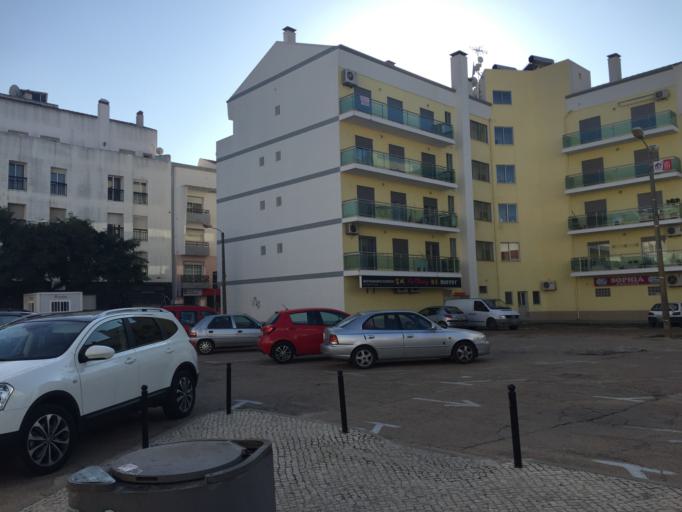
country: PT
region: Faro
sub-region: Vila Real de Santo Antonio
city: Vila Real de Santo Antonio
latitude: 37.1940
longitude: -7.4187
